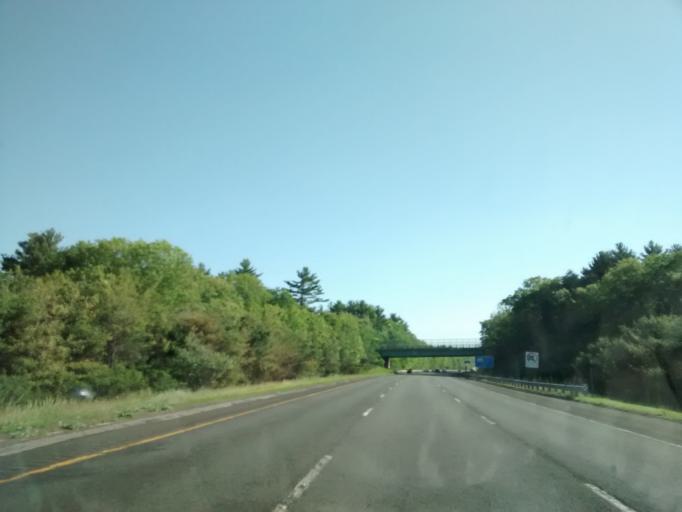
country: US
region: Massachusetts
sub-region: Worcester County
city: Sturbridge
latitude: 42.0956
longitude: -72.0878
